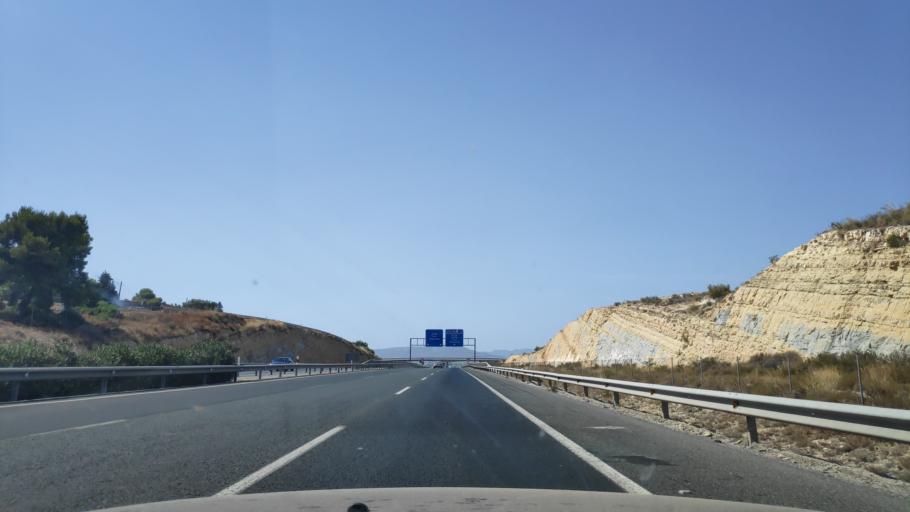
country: ES
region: Murcia
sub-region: Murcia
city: Ulea
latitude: 38.1766
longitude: -1.3139
